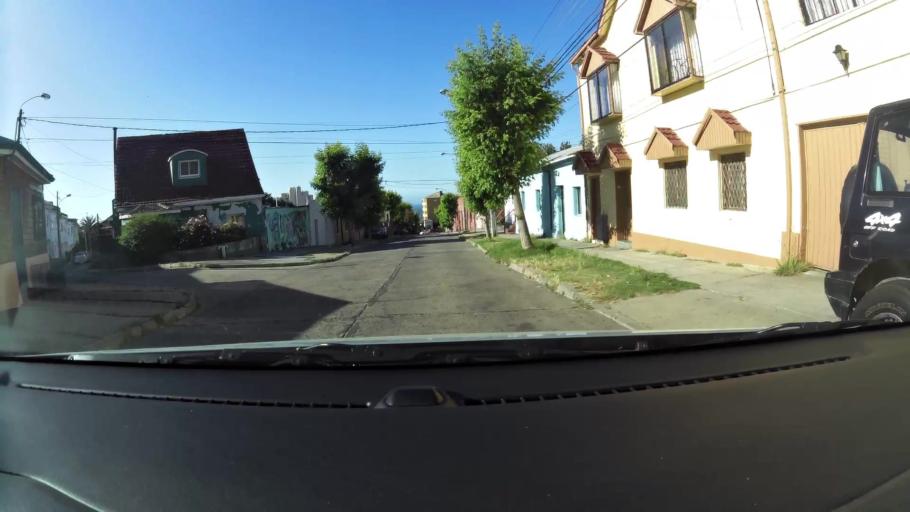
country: CL
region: Valparaiso
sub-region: Provincia de Valparaiso
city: Vina del Mar
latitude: -33.0278
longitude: -71.5687
